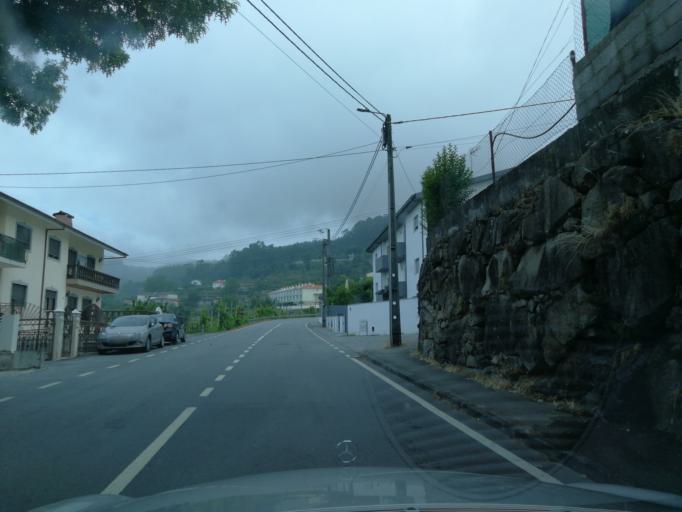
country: PT
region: Braga
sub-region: Guimaraes
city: Ponte
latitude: 41.5160
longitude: -8.3570
